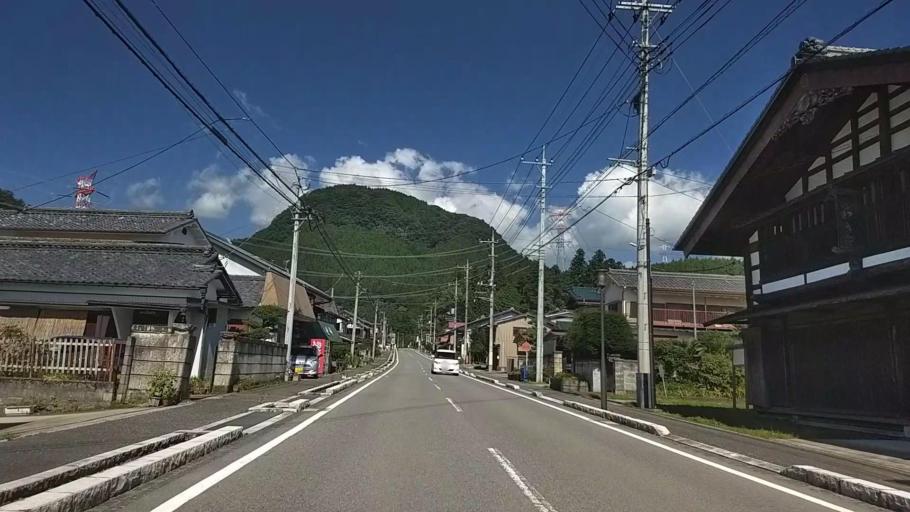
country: JP
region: Gunma
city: Annaka
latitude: 36.3499
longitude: 138.7174
